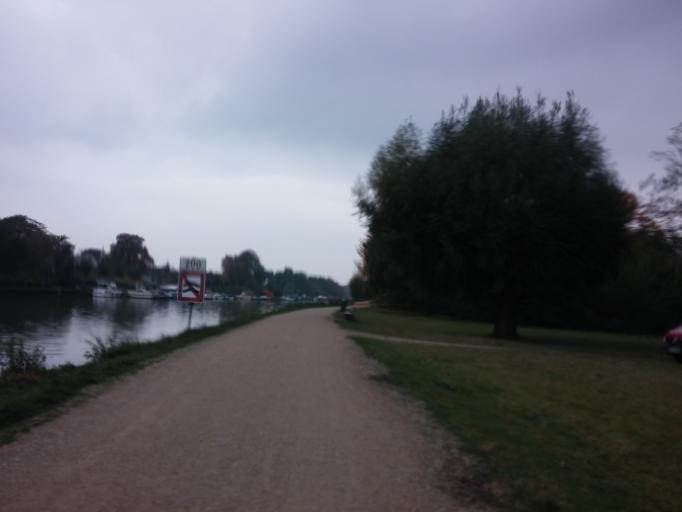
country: DE
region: North Rhine-Westphalia
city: Dorsten
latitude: 51.6643
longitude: 6.9587
